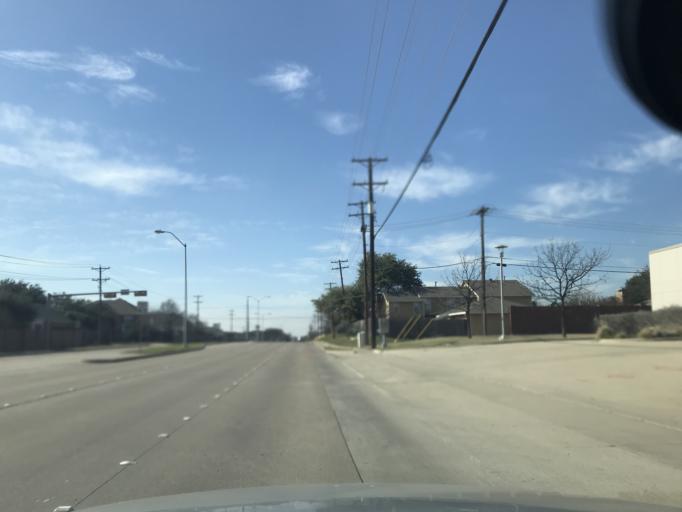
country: US
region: Texas
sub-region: Collin County
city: Plano
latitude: 33.0420
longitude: -96.7723
